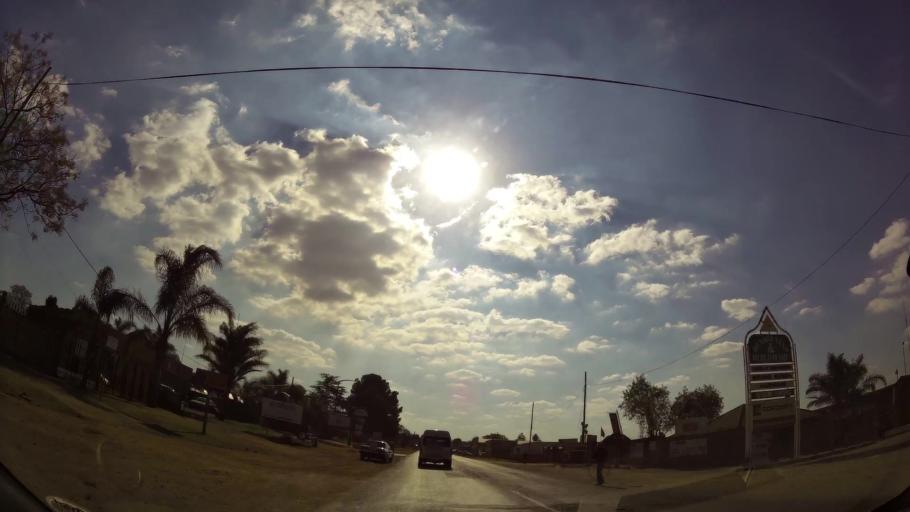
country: ZA
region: Gauteng
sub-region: Ekurhuleni Metropolitan Municipality
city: Benoni
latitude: -26.1287
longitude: 28.3545
